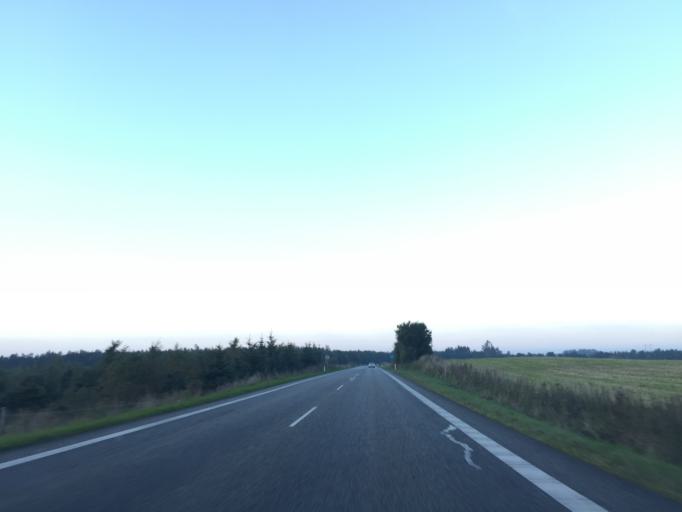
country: DK
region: South Denmark
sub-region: Aabenraa Kommune
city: Lojt Kirkeby
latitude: 55.0885
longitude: 9.4324
